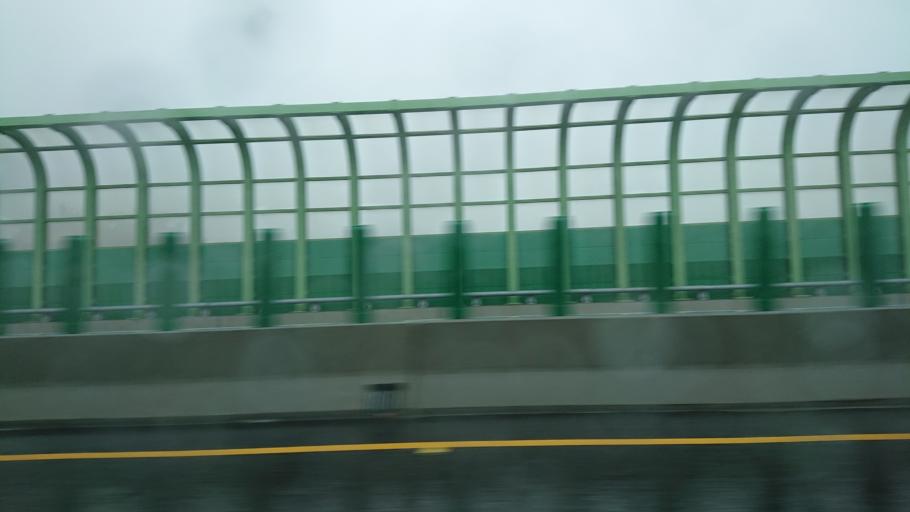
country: TW
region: Taiwan
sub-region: Changhua
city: Chang-hua
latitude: 23.9292
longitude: 120.3147
